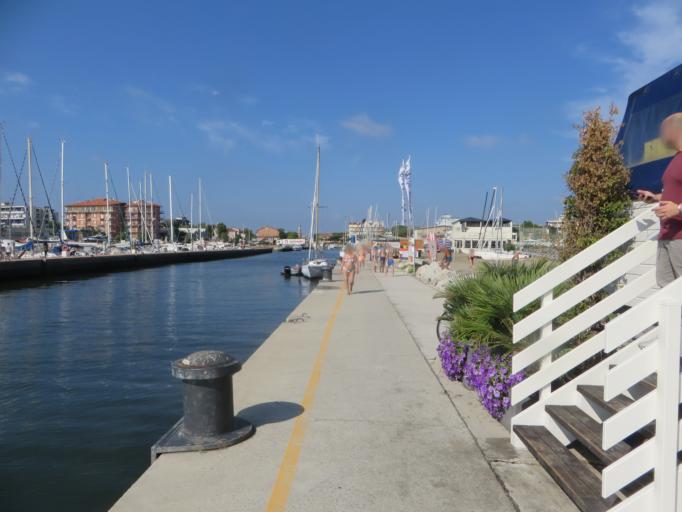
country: IT
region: Emilia-Romagna
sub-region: Provincia di Ravenna
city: Cervia
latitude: 44.2687
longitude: 12.3589
